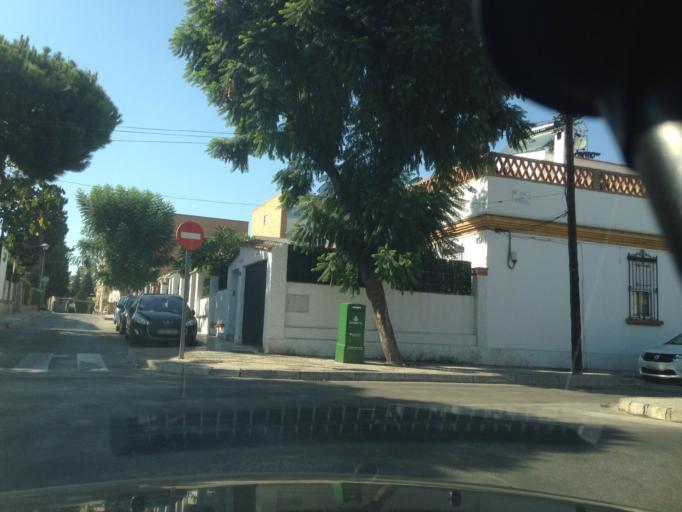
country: ES
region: Andalusia
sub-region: Provincia de Malaga
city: Malaga
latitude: 36.7239
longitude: -4.4568
